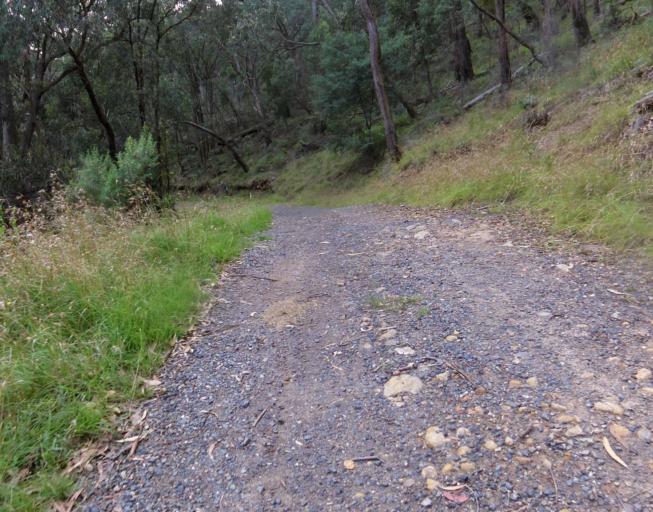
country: AU
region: Victoria
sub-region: Yarra Ranges
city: Montrose
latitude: -37.8311
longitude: 145.3436
